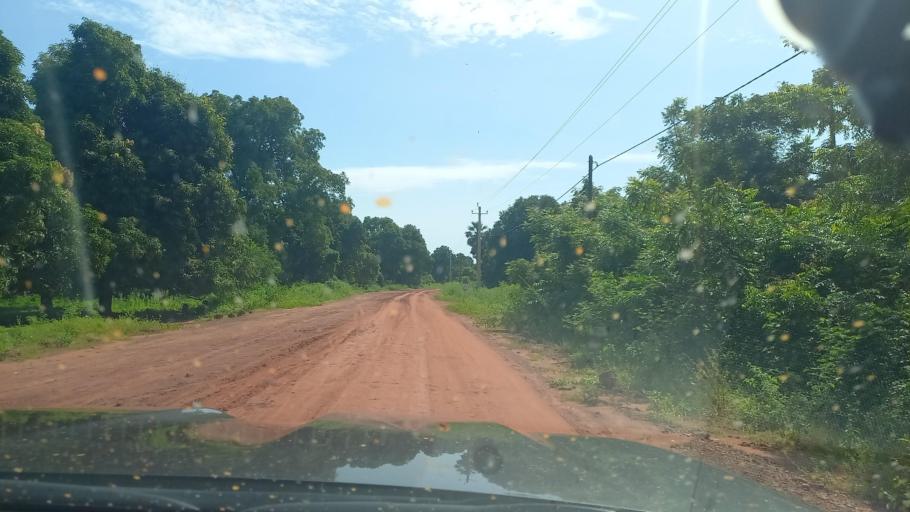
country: SN
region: Ziguinchor
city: Adeane
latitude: 12.6639
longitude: -16.1119
